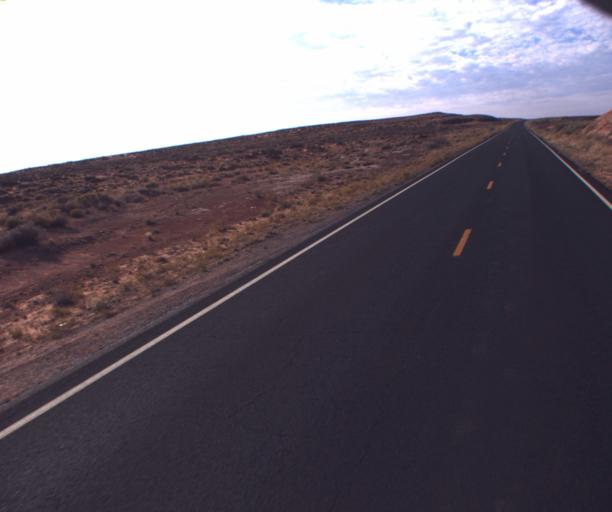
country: US
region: Arizona
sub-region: Apache County
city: Many Farms
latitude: 36.8897
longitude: -109.6272
